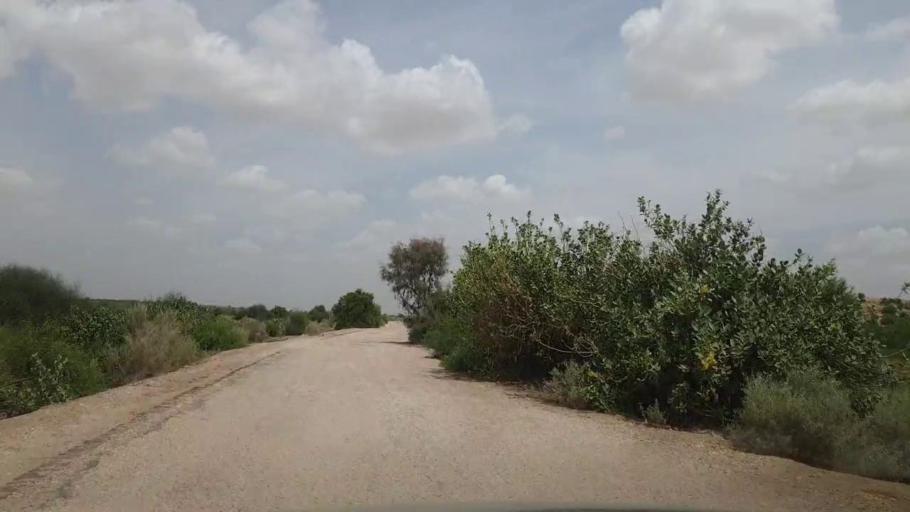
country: PK
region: Sindh
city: Kot Diji
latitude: 27.2035
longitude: 69.1440
